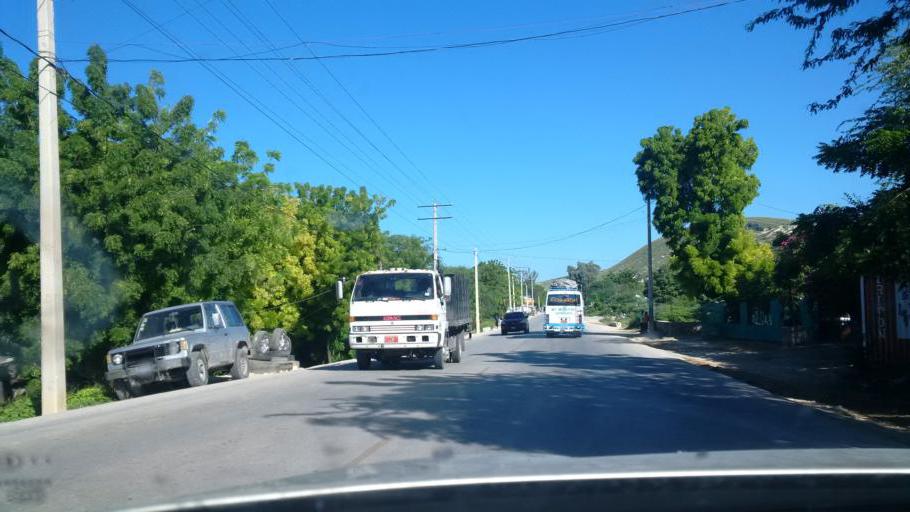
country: HT
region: Ouest
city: Cabaret
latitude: 18.7188
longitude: -72.3702
